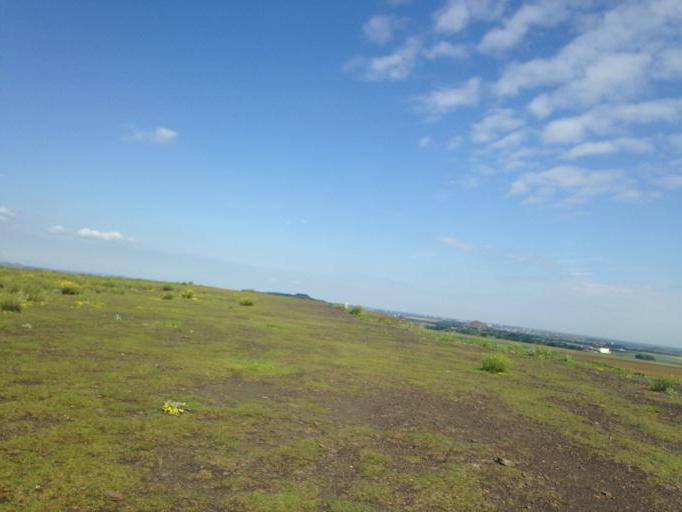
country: FR
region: Nord-Pas-de-Calais
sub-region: Departement du Pas-de-Calais
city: Loos-en-Gohelle
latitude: 50.4480
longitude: 2.7810
